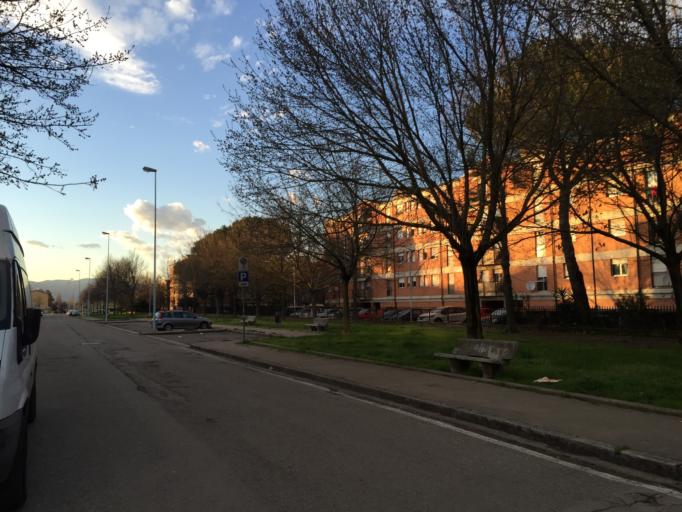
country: IT
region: Tuscany
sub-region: Provincia di Prato
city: Fornacelle
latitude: 43.8872
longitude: 11.0507
